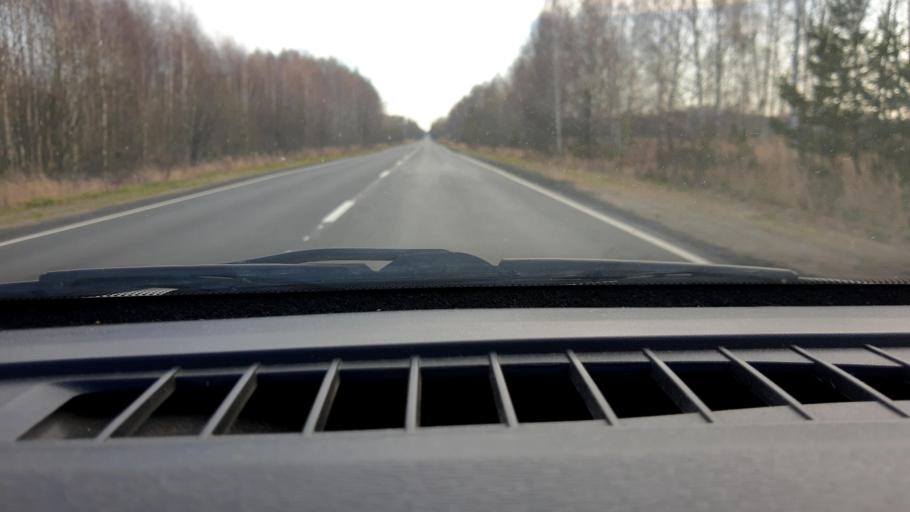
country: RU
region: Nizjnij Novgorod
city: Novaya Balakhna
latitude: 56.5722
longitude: 43.7073
